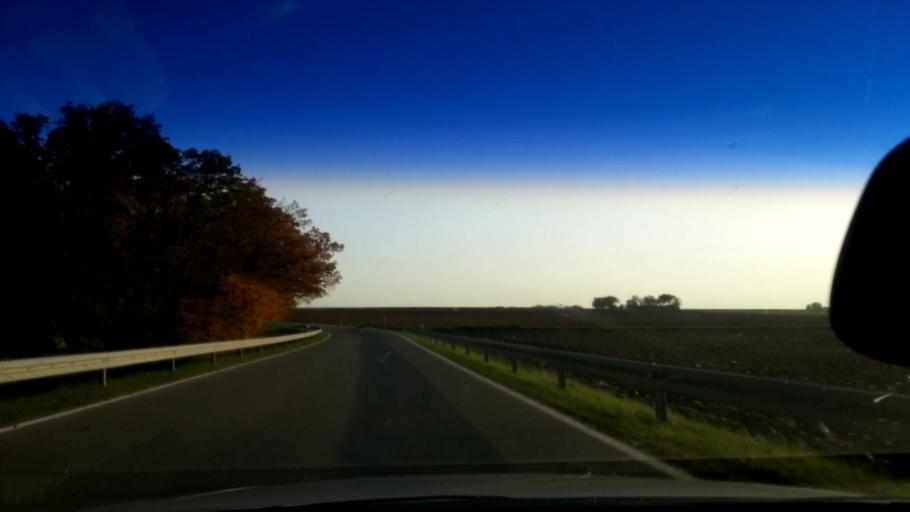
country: DE
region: Bavaria
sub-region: Upper Franconia
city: Memmelsdorf
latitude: 49.9792
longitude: 10.9679
